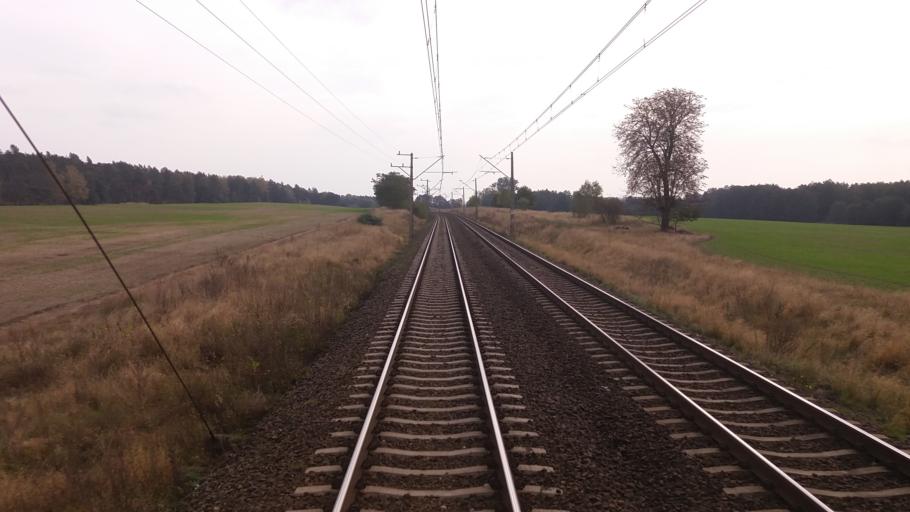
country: PL
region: West Pomeranian Voivodeship
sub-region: Powiat stargardzki
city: Dolice
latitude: 53.2124
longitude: 15.1647
